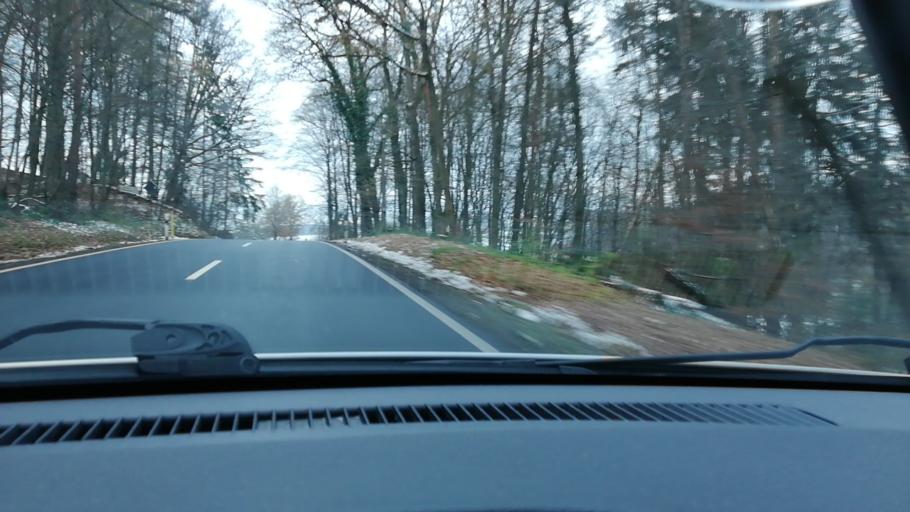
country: DE
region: Bavaria
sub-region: Regierungsbezirk Unterfranken
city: Krombach
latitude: 50.1042
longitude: 9.2234
